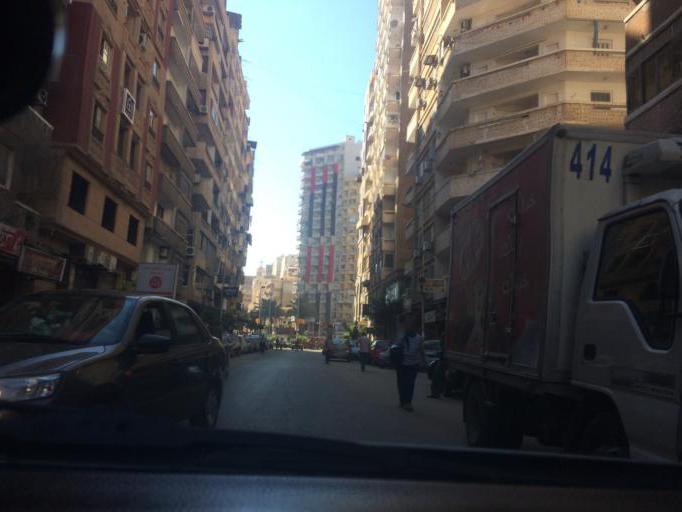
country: EG
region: Alexandria
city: Alexandria
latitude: 31.2612
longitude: 29.9945
